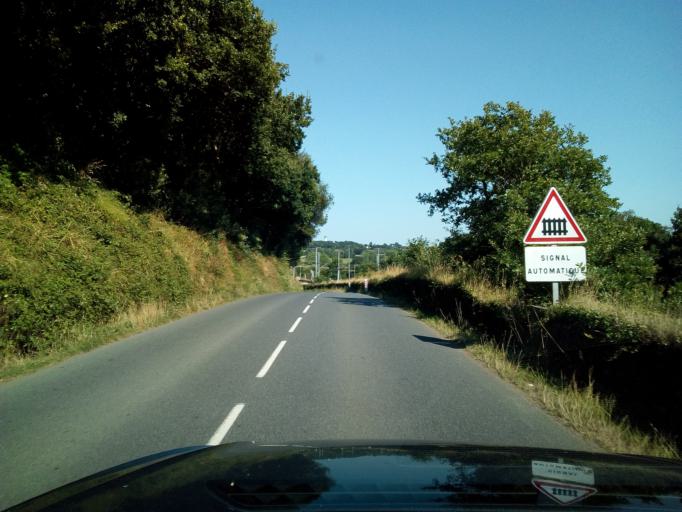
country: FR
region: Brittany
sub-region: Departement du Finistere
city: Landivisiau
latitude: 48.4962
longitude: -4.0860
